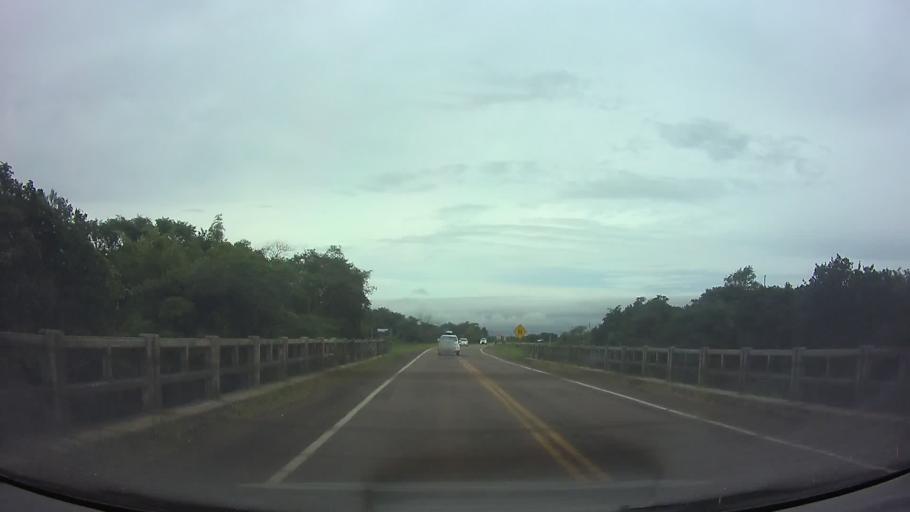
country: PY
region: Paraguari
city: Carapegua
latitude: -25.7263
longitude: -57.2052
